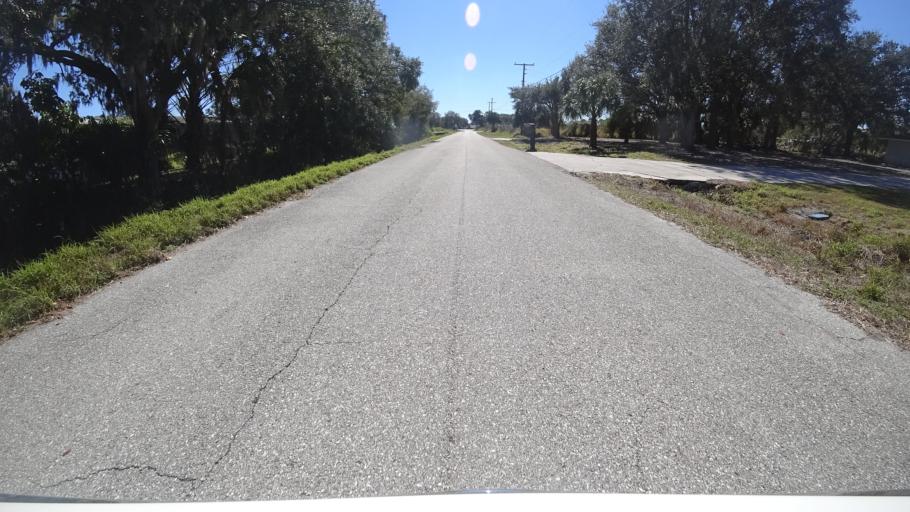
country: US
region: Florida
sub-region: Manatee County
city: Memphis
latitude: 27.5694
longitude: -82.5483
